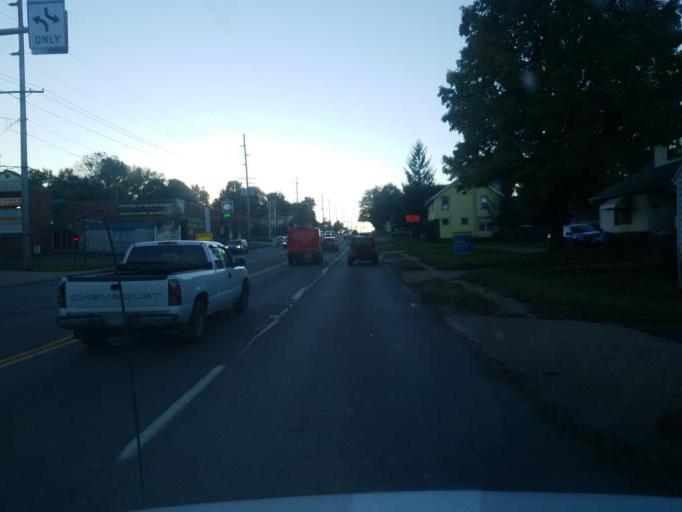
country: US
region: Ohio
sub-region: Stark County
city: Canton
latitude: 40.8307
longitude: -81.3537
